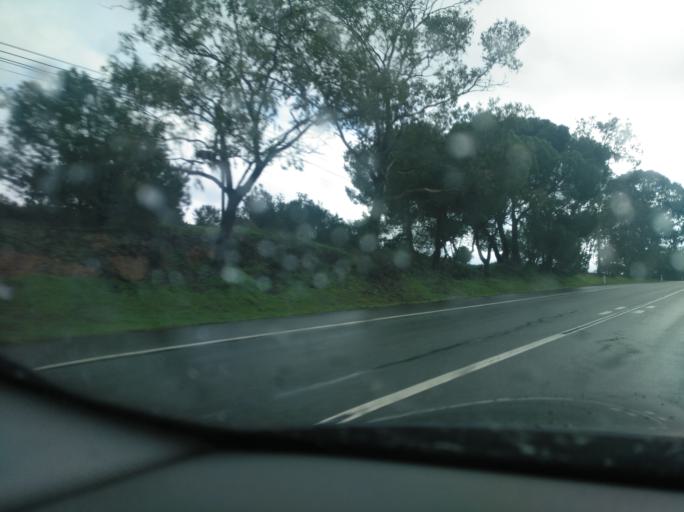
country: PT
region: Setubal
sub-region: Grandola
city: Grandola
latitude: 38.1044
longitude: -8.4183
